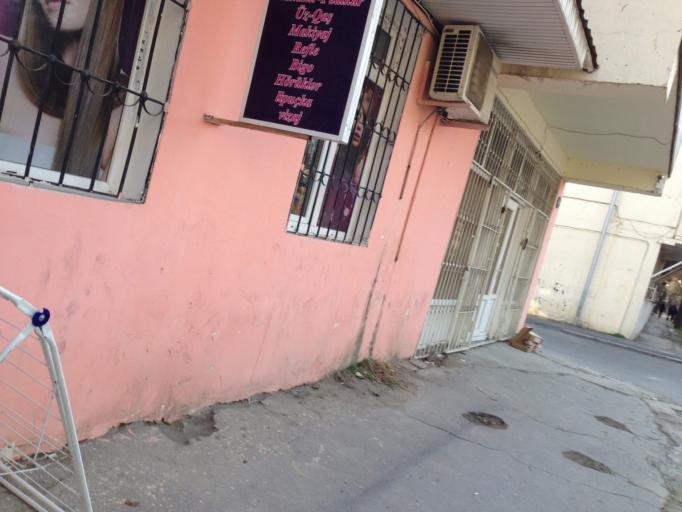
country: AZ
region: Baki
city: Baku
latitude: 40.3951
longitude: 49.8732
